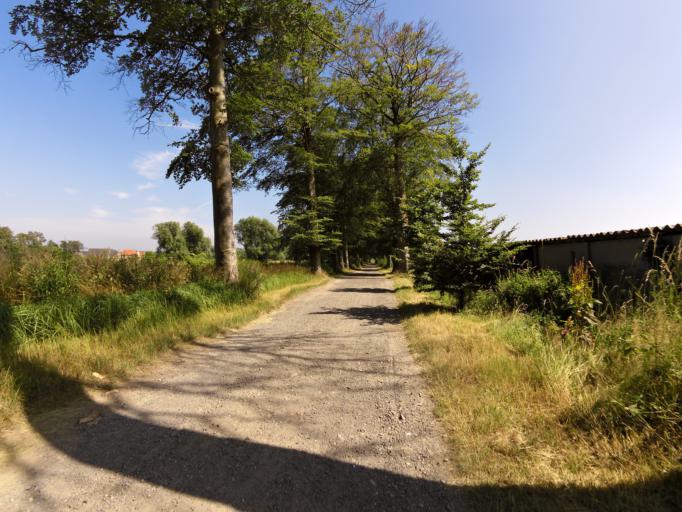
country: BE
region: Flanders
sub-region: Provincie West-Vlaanderen
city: Zedelgem
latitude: 51.1542
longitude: 3.1358
